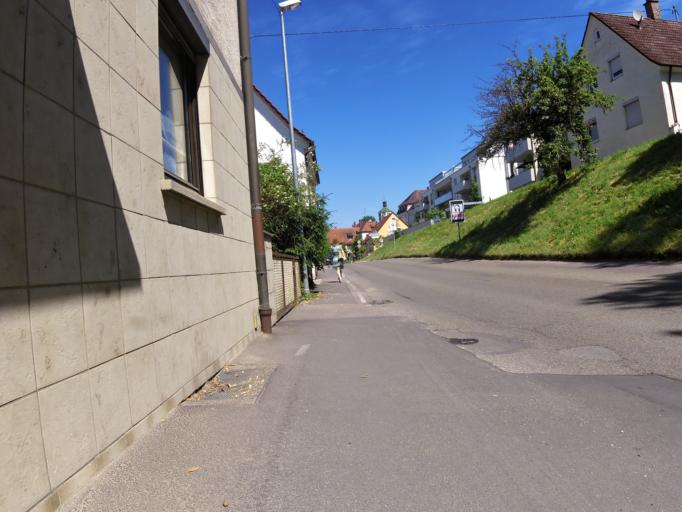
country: DE
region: Bavaria
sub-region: Swabia
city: Guenzburg
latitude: 48.4524
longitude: 10.2757
